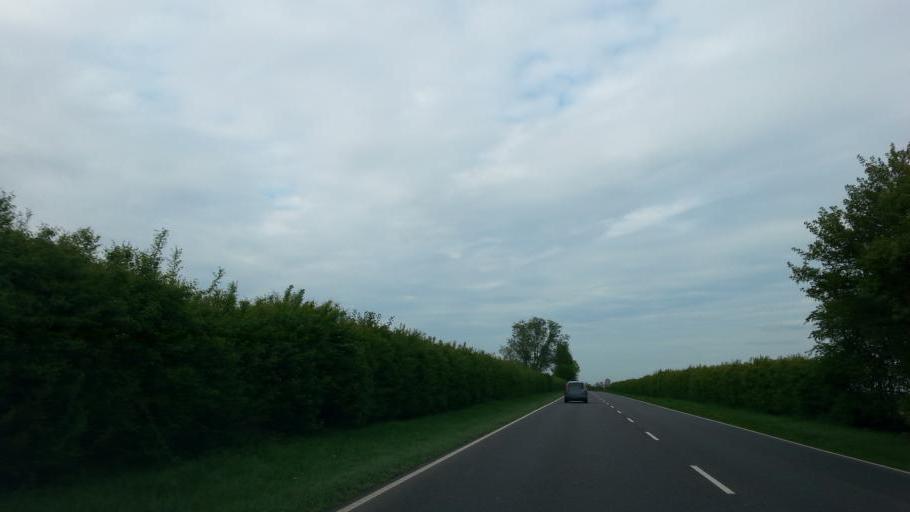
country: GB
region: England
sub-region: Cambridgeshire
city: Doddington
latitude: 52.4960
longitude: 0.0745
